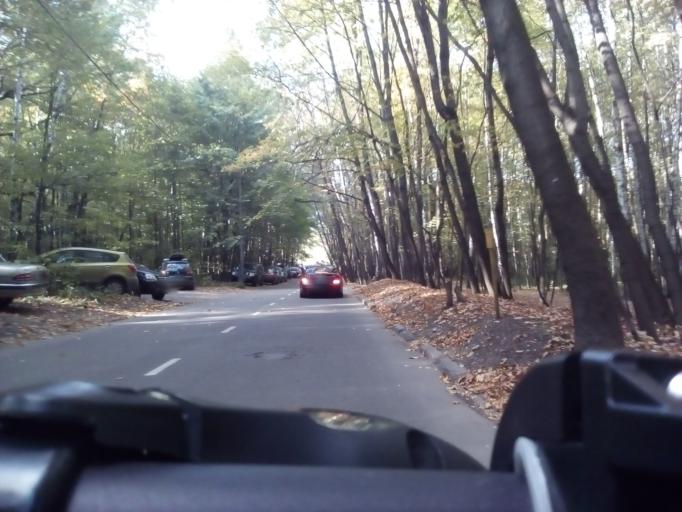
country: RU
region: Moscow
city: Sokol'niki
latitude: 55.8086
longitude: 37.6673
